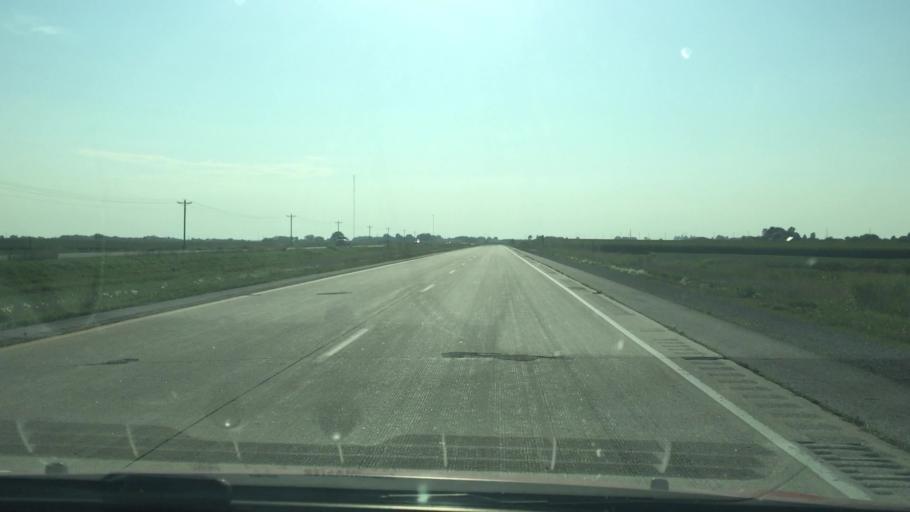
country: US
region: Iowa
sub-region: Cedar County
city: Durant
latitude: 41.5197
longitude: -90.8630
